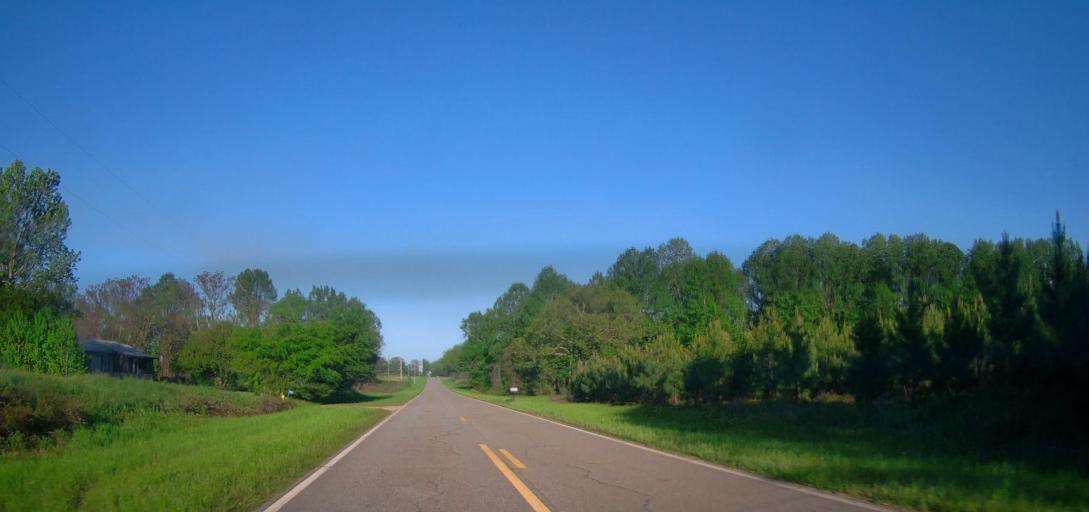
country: US
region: Georgia
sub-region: Macon County
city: Oglethorpe
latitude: 32.3019
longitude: -84.0973
